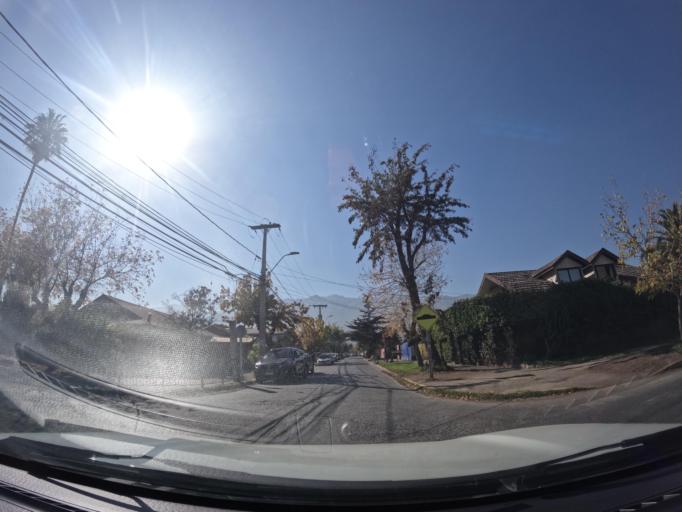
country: CL
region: Santiago Metropolitan
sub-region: Provincia de Santiago
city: Villa Presidente Frei, Nunoa, Santiago, Chile
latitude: -33.4659
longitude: -70.5712
